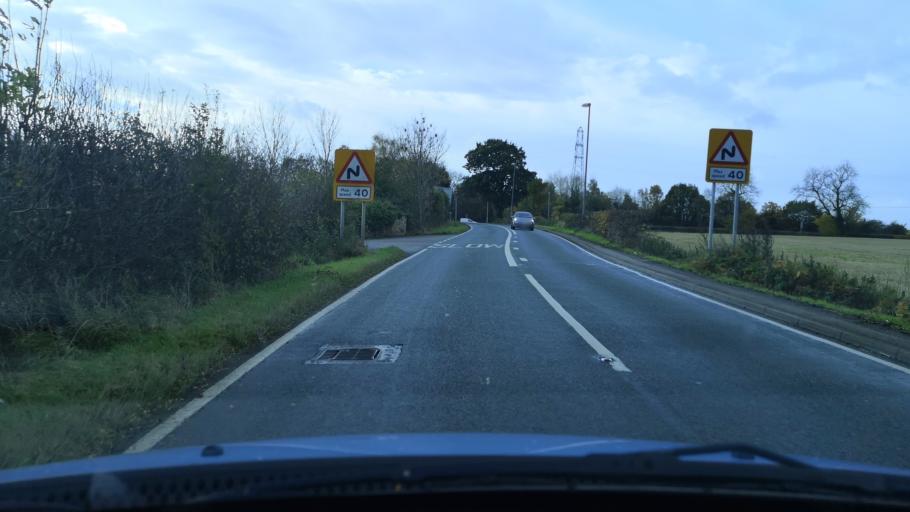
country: GB
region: England
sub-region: City and Borough of Wakefield
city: Ryhill
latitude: 53.6148
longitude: -1.4253
